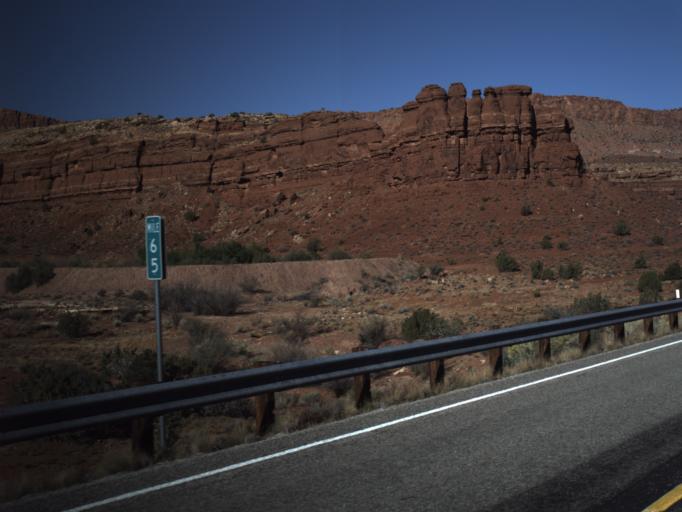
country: US
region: Utah
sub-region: San Juan County
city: Blanding
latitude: 37.7014
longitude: -110.2345
